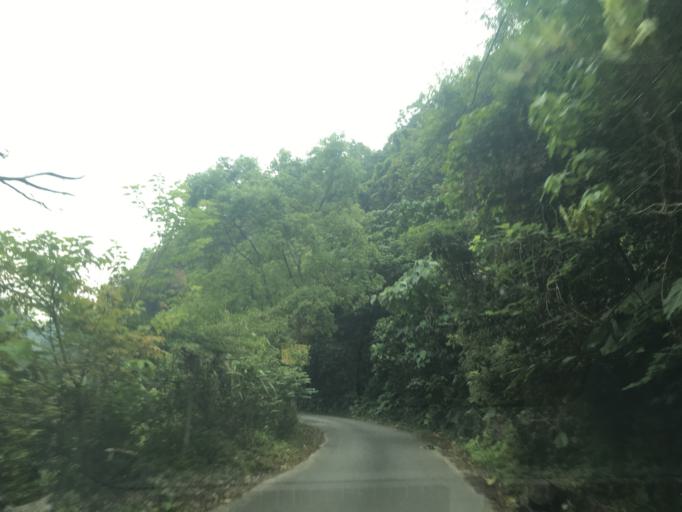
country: TW
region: Taiwan
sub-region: Taichung City
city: Taichung
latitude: 24.0578
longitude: 120.7731
